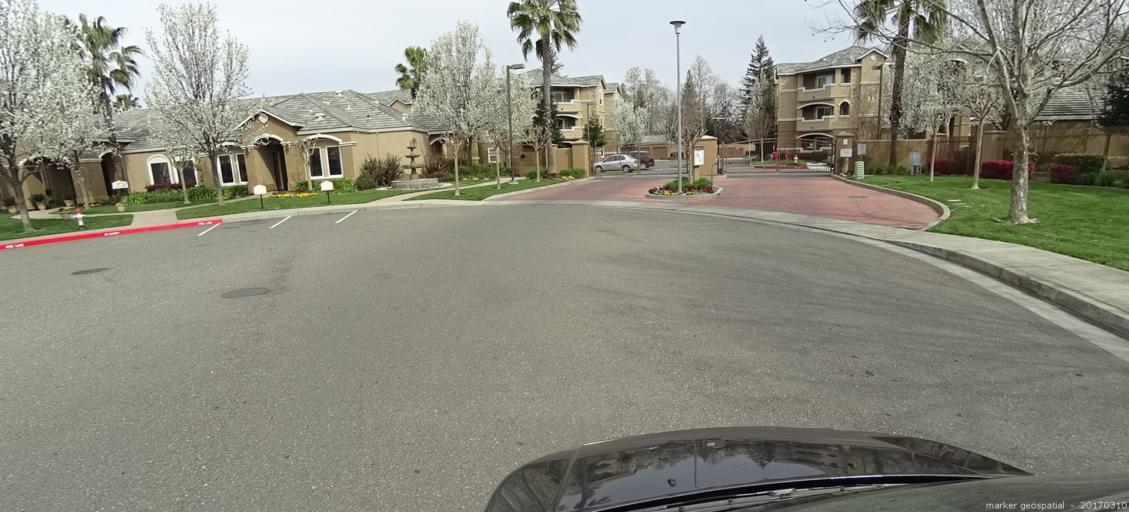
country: US
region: California
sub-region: Sacramento County
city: Parkway
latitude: 38.4935
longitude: -121.5183
